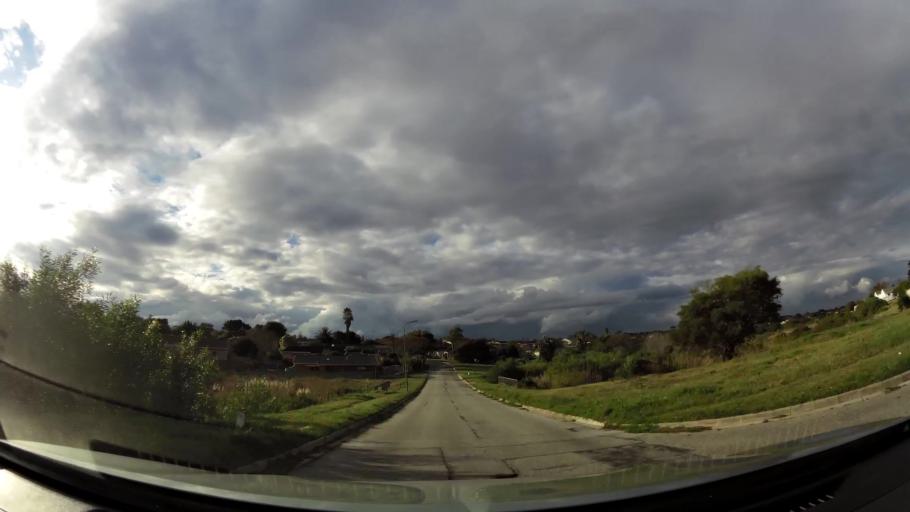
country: ZA
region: Eastern Cape
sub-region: Nelson Mandela Bay Metropolitan Municipality
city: Port Elizabeth
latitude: -33.9503
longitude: 25.4800
